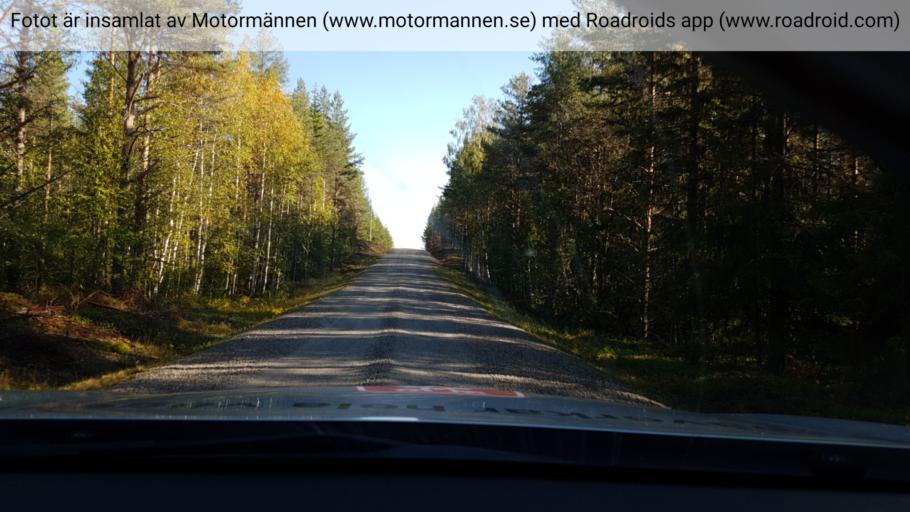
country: SE
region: Vaesterbotten
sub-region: Norsjo Kommun
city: Norsjoe
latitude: 64.6945
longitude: 19.4390
